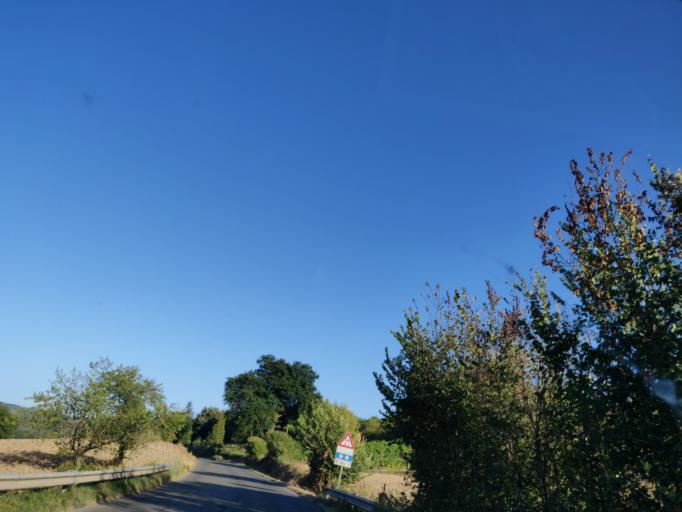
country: IT
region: Latium
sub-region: Provincia di Viterbo
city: Acquapendente
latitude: 42.7622
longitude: 11.8572
